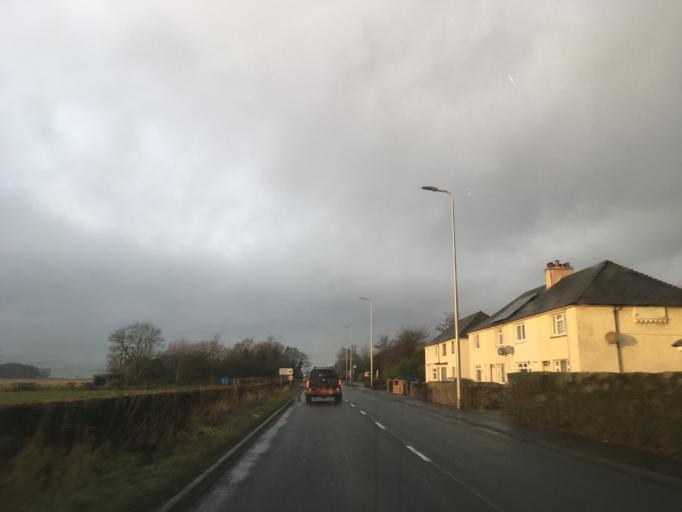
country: GB
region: Scotland
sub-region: Stirling
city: Cowie
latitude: 56.0990
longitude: -3.8429
